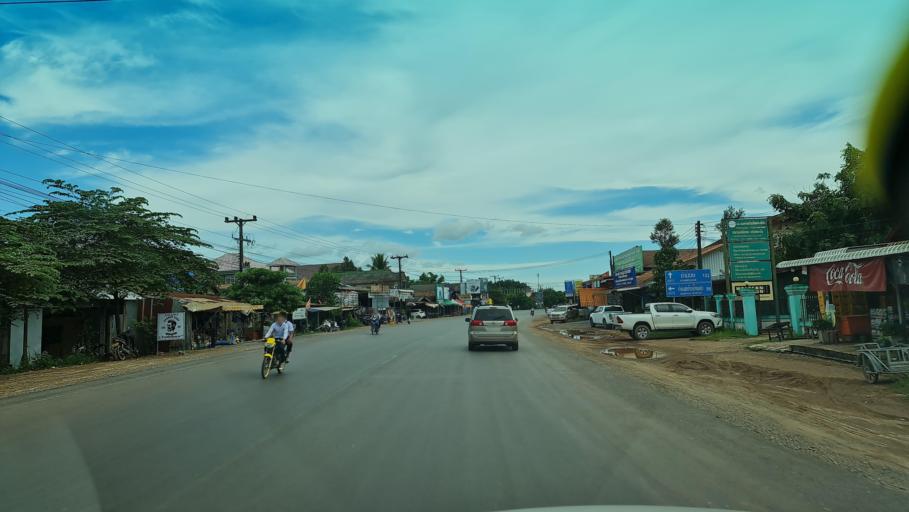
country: TH
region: Nakhon Phanom
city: Ban Phaeng
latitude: 18.0996
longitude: 104.2862
